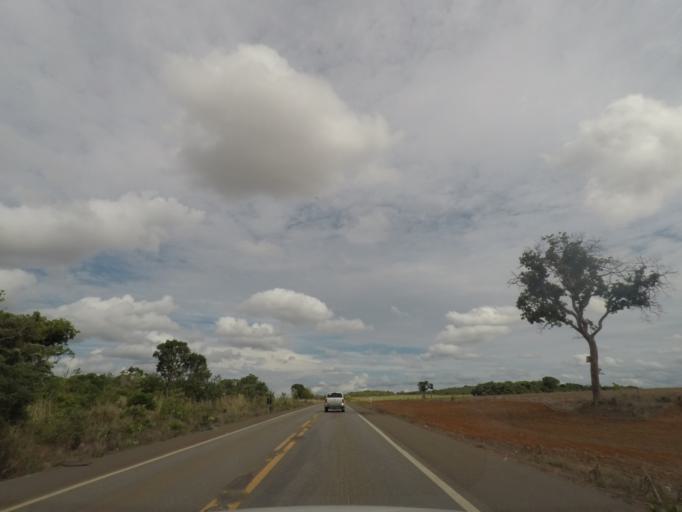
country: BR
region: Goias
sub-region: Uruacu
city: Uruacu
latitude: -14.6691
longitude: -49.1452
